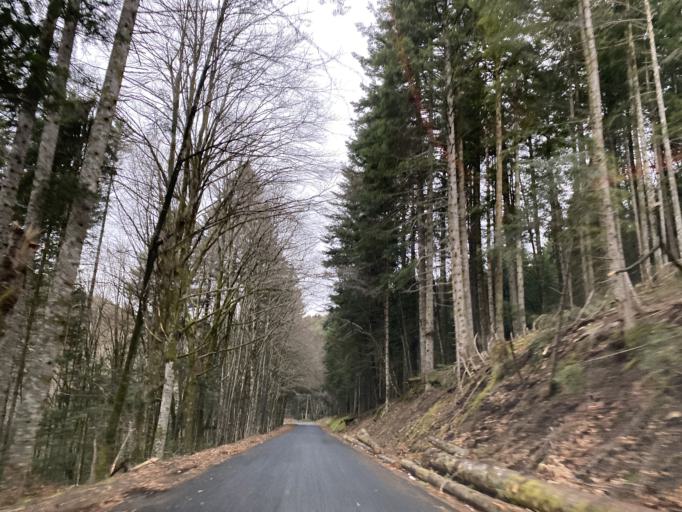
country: FR
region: Rhone-Alpes
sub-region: Departement de la Loire
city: Noiretable
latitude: 45.7334
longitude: 3.7386
